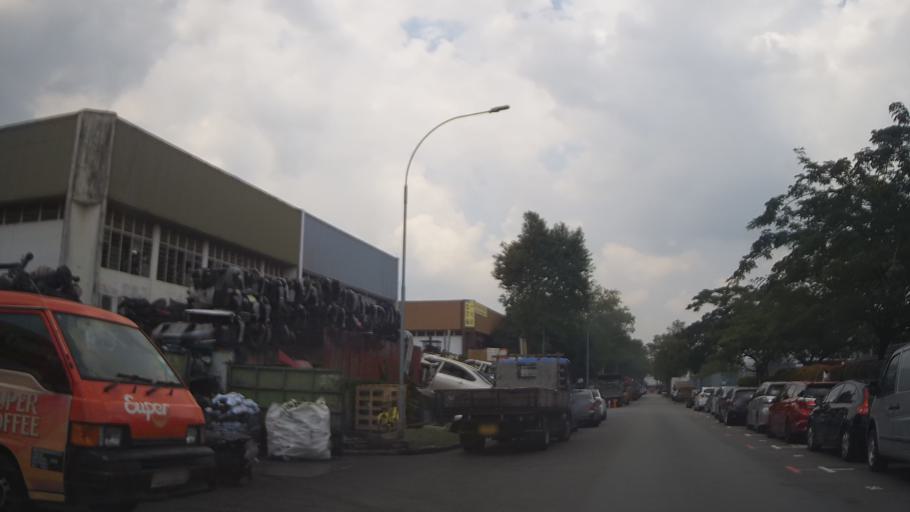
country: MY
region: Johor
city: Johor Bahru
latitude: 1.4510
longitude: 103.7964
